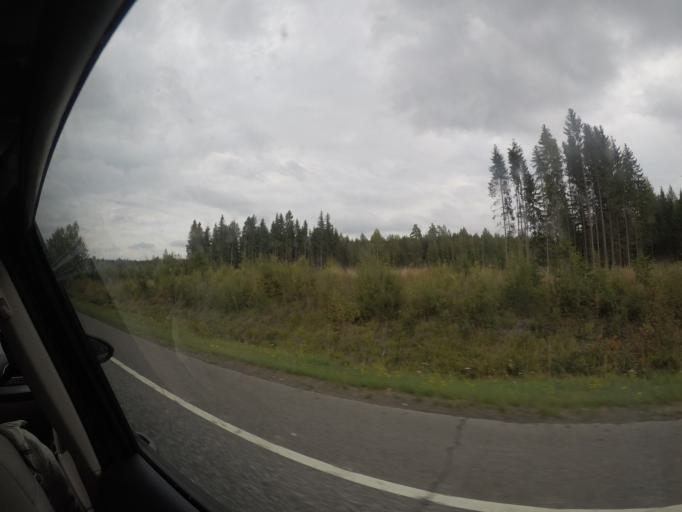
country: FI
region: Haeme
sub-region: Haemeenlinna
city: Parola
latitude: 61.1776
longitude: 24.4124
